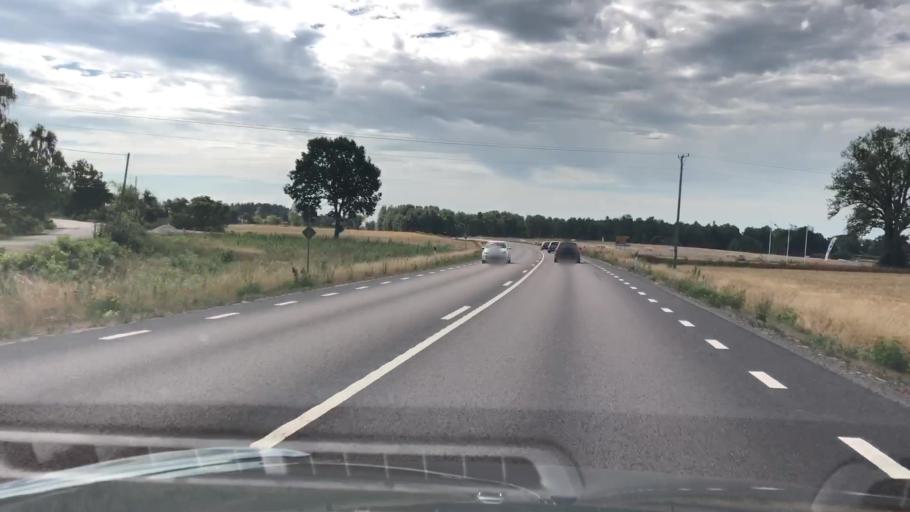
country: SE
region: Kalmar
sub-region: Torsas Kommun
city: Torsas
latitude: 56.3680
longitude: 16.0641
